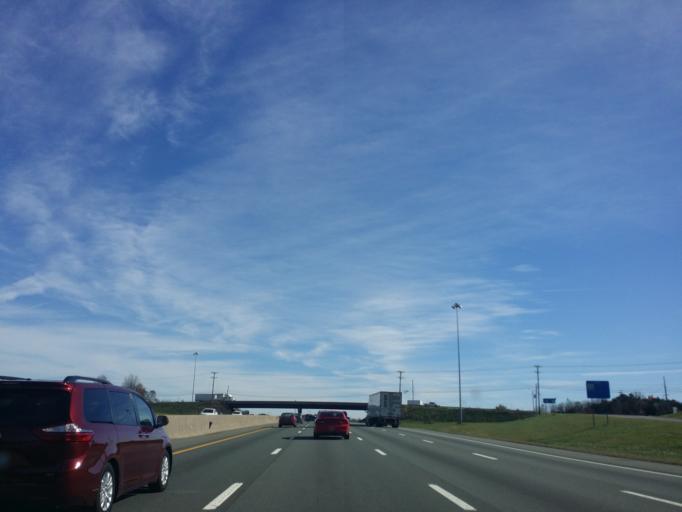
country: US
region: North Carolina
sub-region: Alamance County
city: Haw River
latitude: 36.0687
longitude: -79.3561
